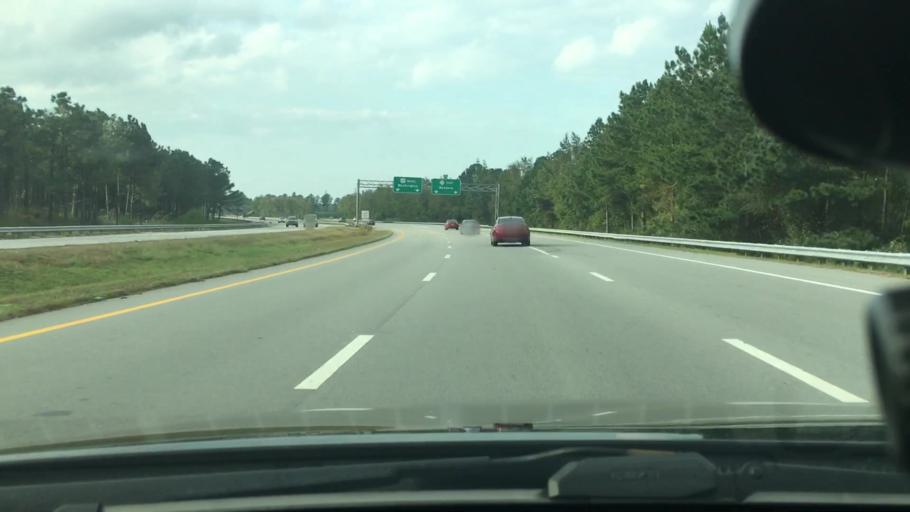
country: US
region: North Carolina
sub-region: Craven County
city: James City
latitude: 35.1102
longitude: -77.0087
